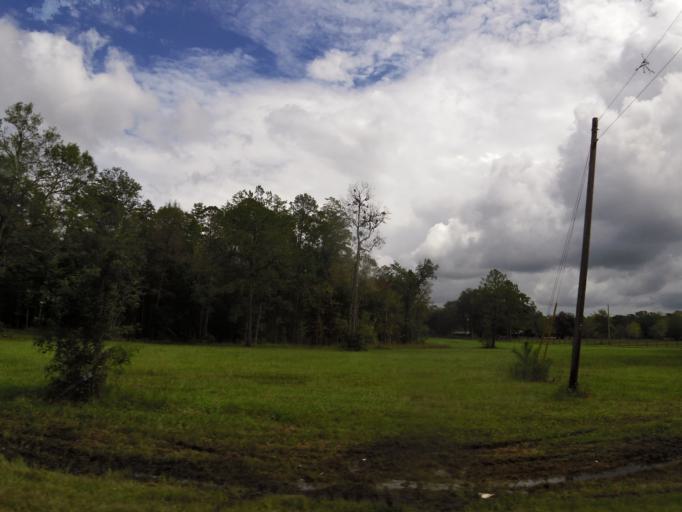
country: US
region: Florida
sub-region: Clay County
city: Middleburg
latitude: 30.1234
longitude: -81.9989
